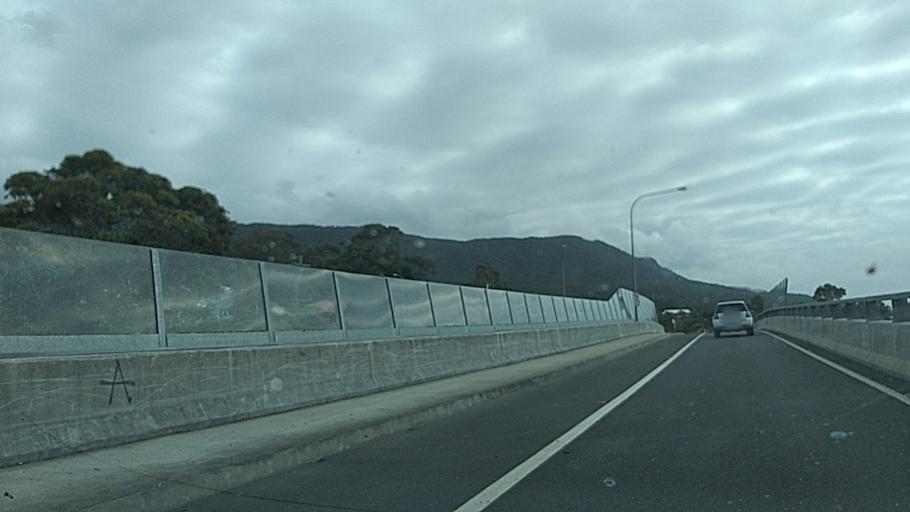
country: AU
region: New South Wales
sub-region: Wollongong
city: Bulli
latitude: -34.3232
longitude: 150.9129
